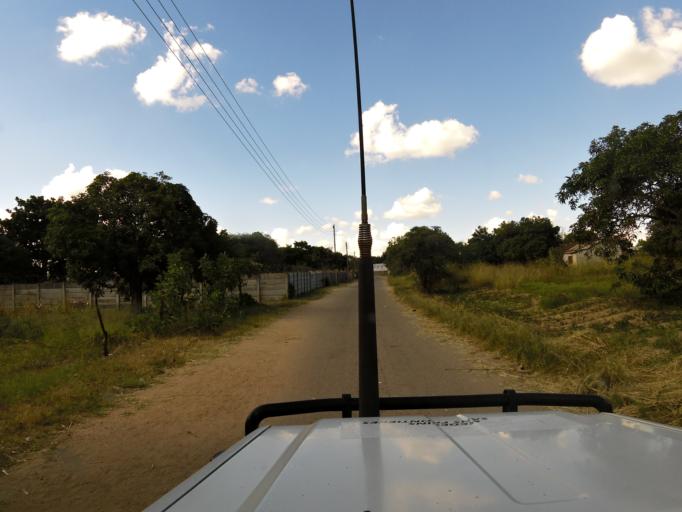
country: ZW
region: Harare
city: Epworth
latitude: -17.8712
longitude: 31.1300
